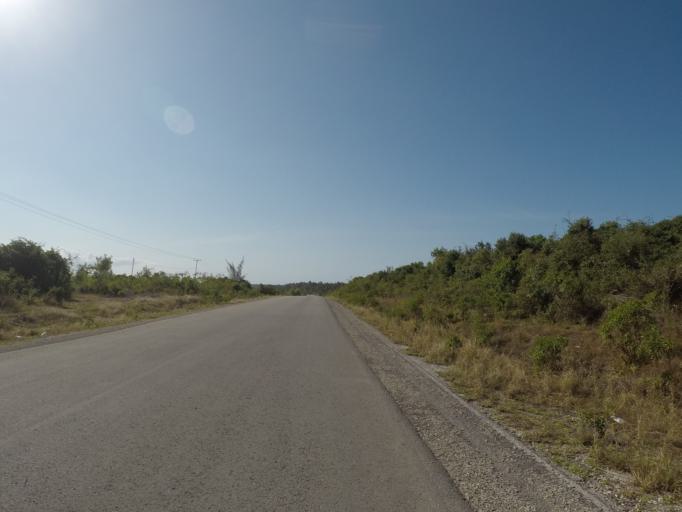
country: TZ
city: Kiwengwa
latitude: -6.1586
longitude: 39.5196
